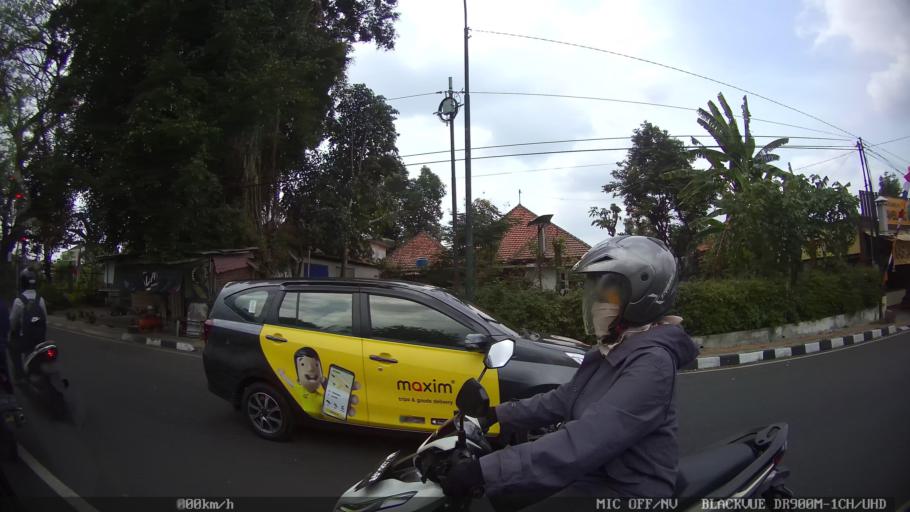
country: ID
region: Daerah Istimewa Yogyakarta
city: Yogyakarta
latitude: -7.7877
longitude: 110.3786
